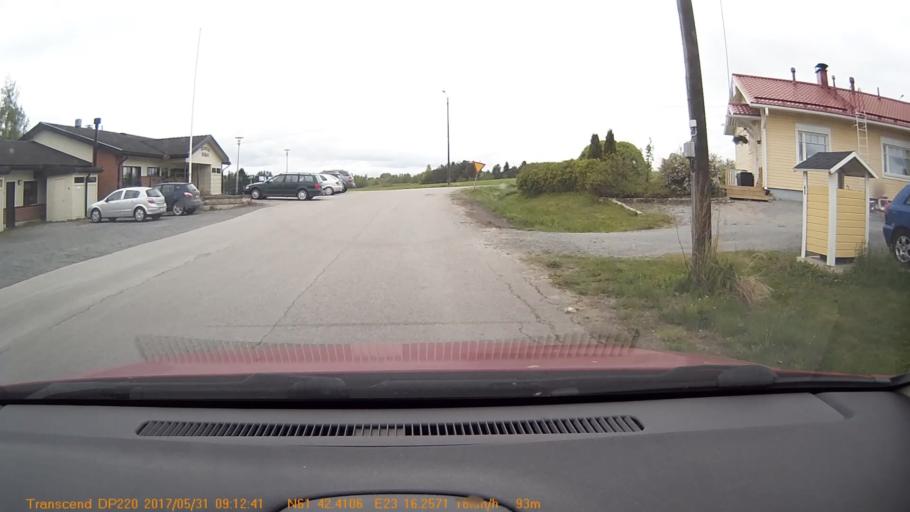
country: FI
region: Pirkanmaa
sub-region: Tampere
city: Viljakkala
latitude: 61.7068
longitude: 23.2711
